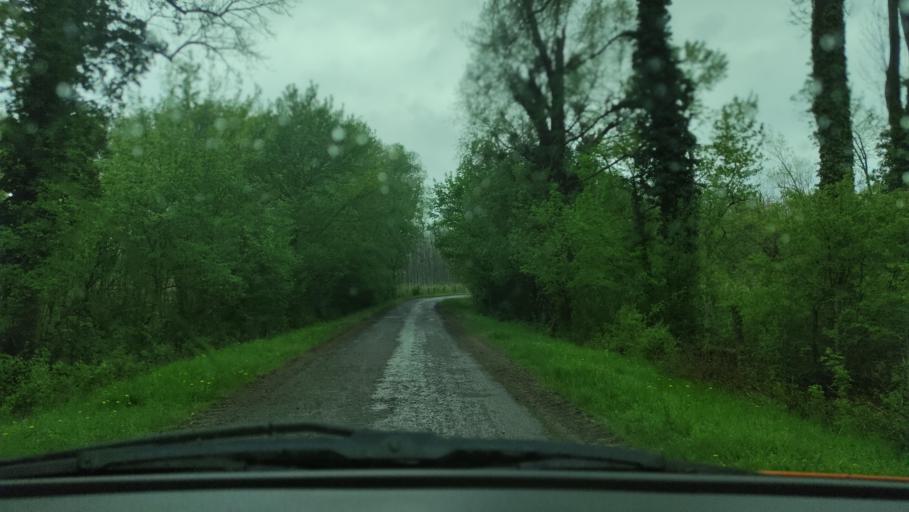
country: HU
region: Baranya
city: Mohacs
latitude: 45.9094
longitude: 18.7552
